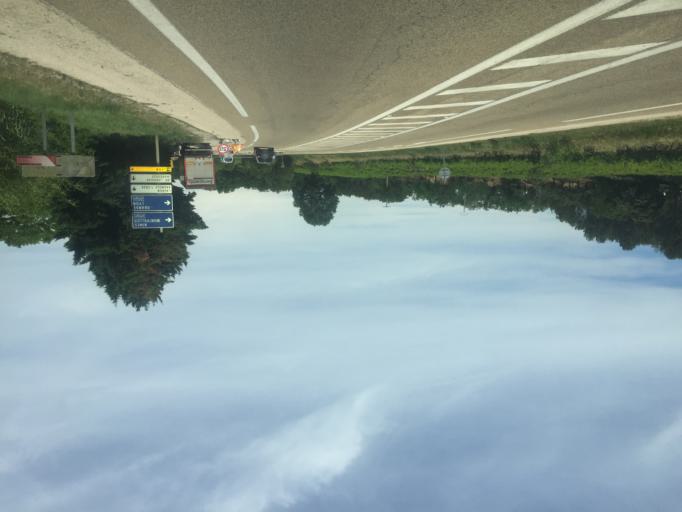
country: FR
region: Languedoc-Roussillon
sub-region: Departement du Gard
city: Tavel
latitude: 44.0258
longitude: 4.7372
